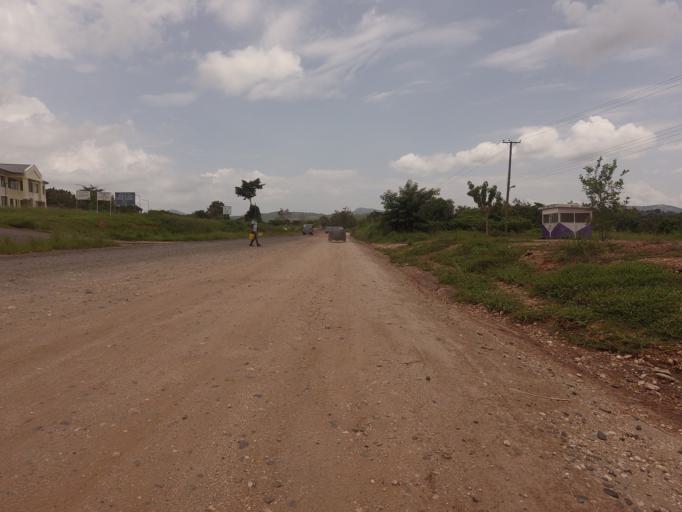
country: GH
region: Volta
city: Ho
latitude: 6.6790
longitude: 0.3187
